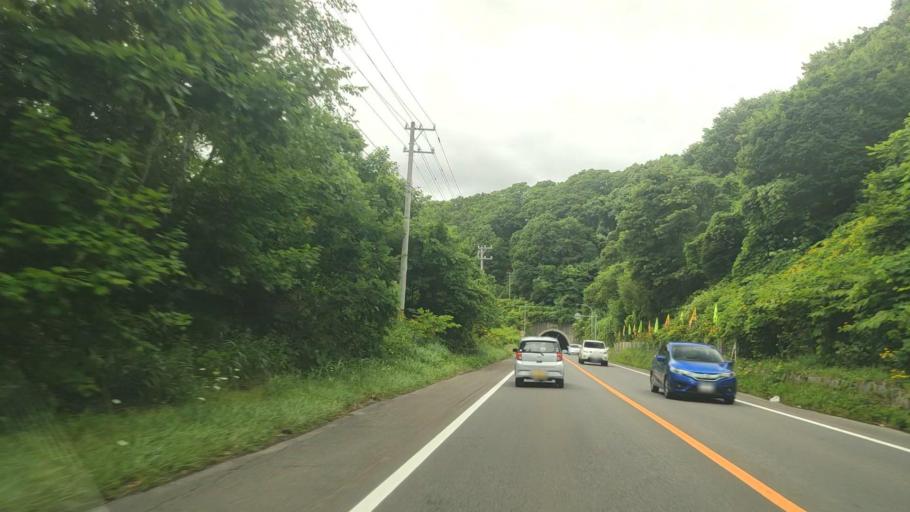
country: JP
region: Hokkaido
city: Date
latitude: 42.5693
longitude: 140.7349
